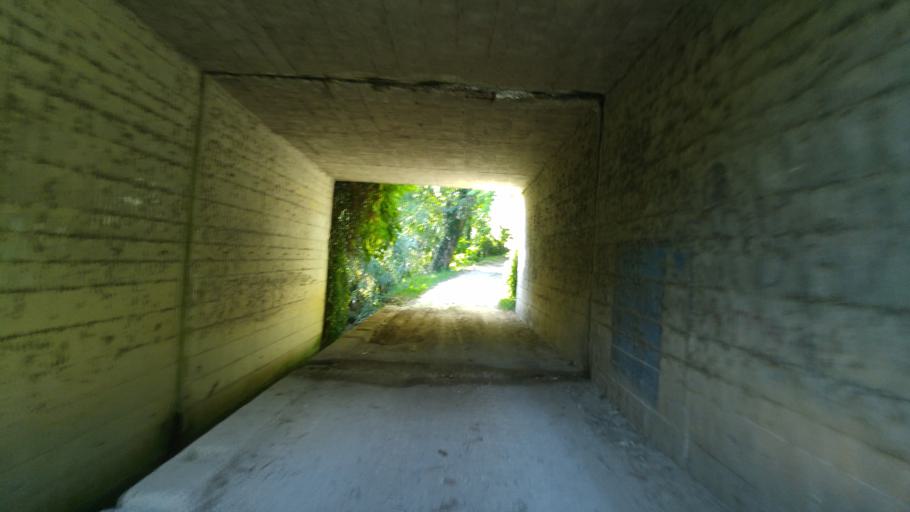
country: IT
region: The Marches
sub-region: Provincia di Pesaro e Urbino
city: Calcinelli
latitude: 43.7509
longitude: 12.9258
